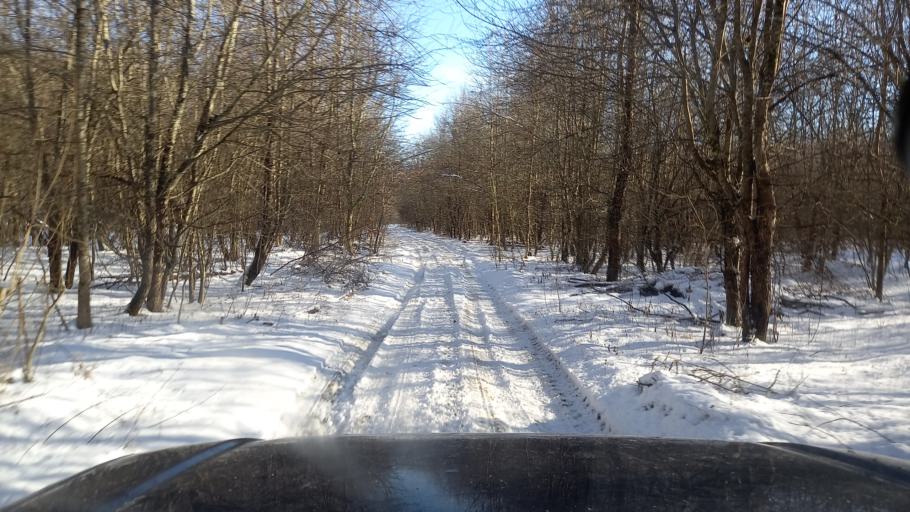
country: RU
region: Adygeya
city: Kamennomostskiy
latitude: 44.2113
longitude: 40.1420
